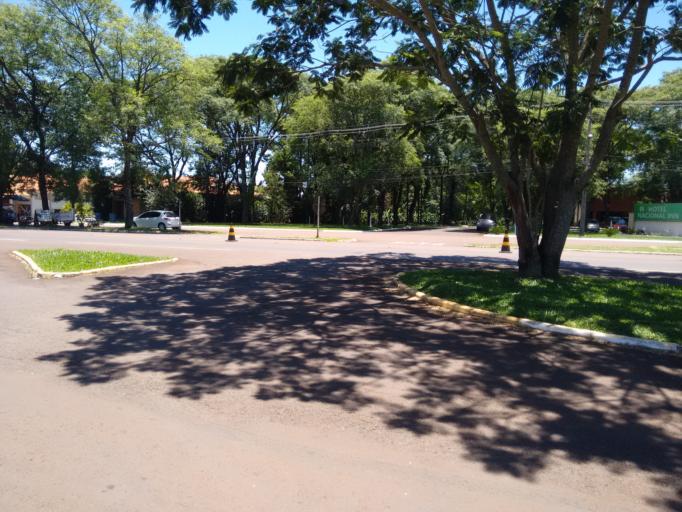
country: AR
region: Misiones
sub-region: Departamento de Iguazu
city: Puerto Iguazu
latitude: -25.5913
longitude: -54.5167
